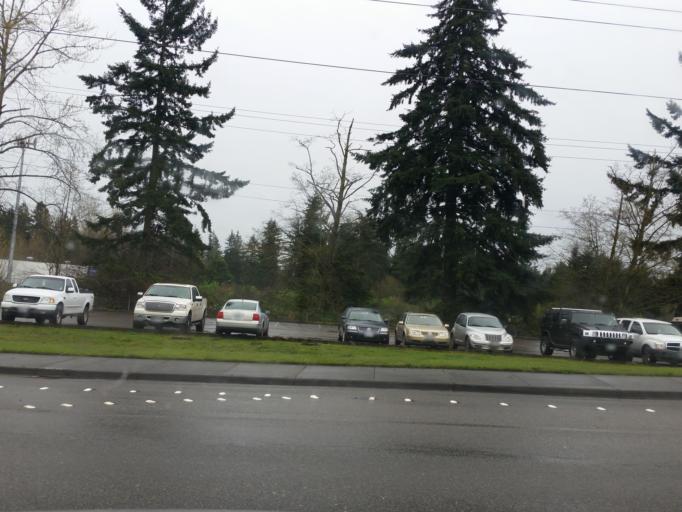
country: US
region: Washington
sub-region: Snohomish County
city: Martha Lake
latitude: 47.8786
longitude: -122.2397
